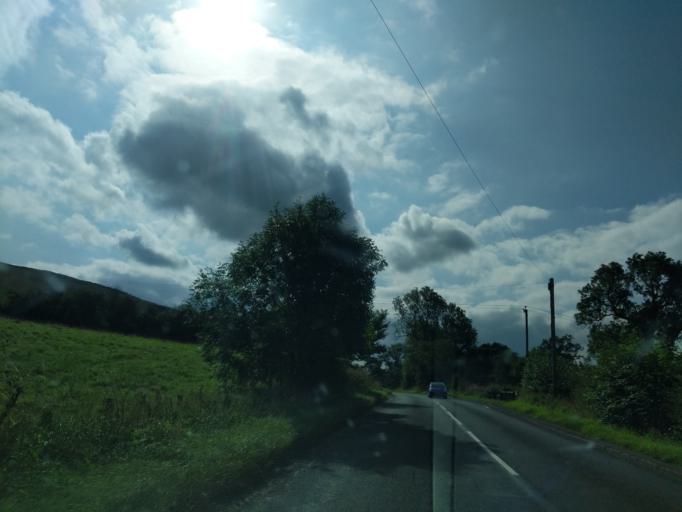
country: GB
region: Scotland
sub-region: The Scottish Borders
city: Peebles
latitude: 55.6834
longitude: -3.2100
